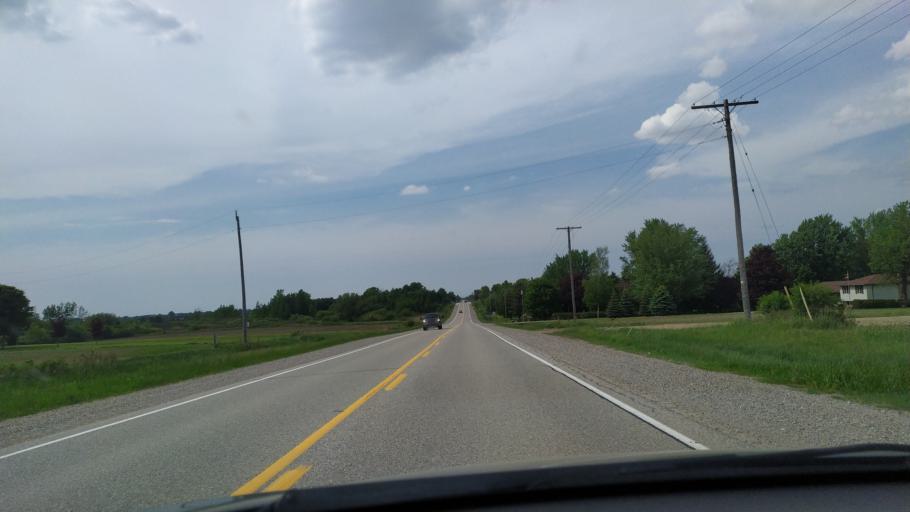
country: CA
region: Ontario
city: Stratford
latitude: 43.2113
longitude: -81.0666
